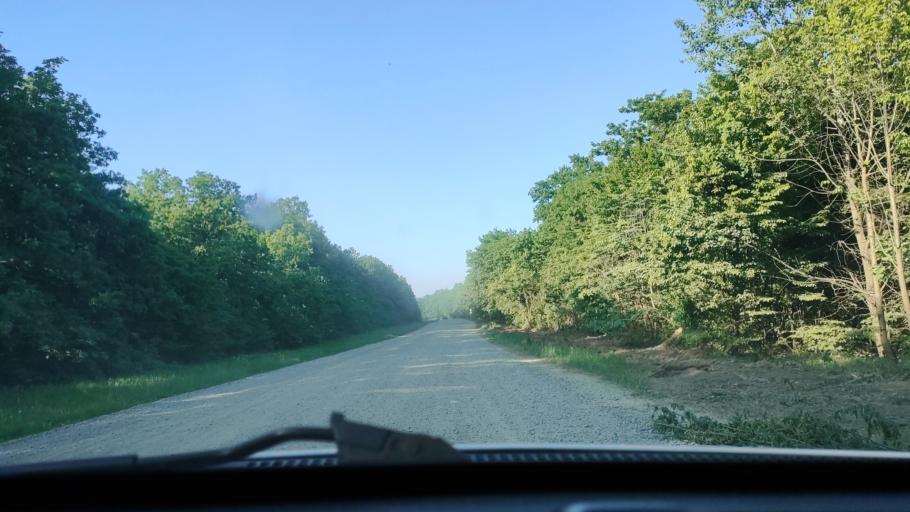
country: RU
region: Krasnodarskiy
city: Goryachiy Klyuch
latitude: 44.7046
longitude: 38.9892
